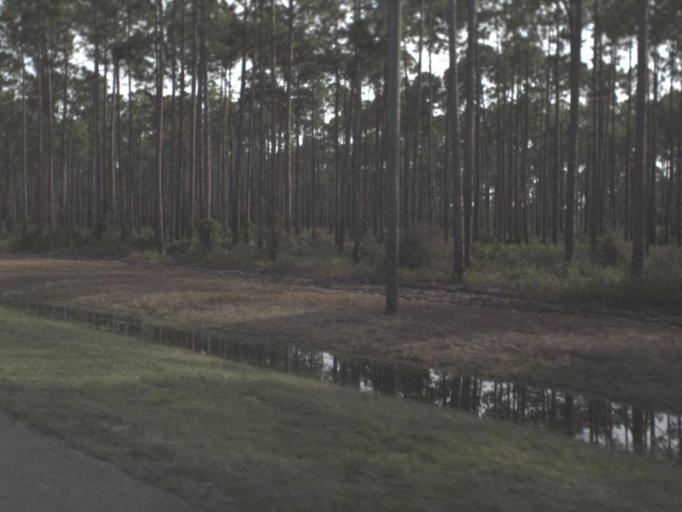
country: US
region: Florida
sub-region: Bay County
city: Mexico Beach
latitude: 29.9859
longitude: -85.4813
